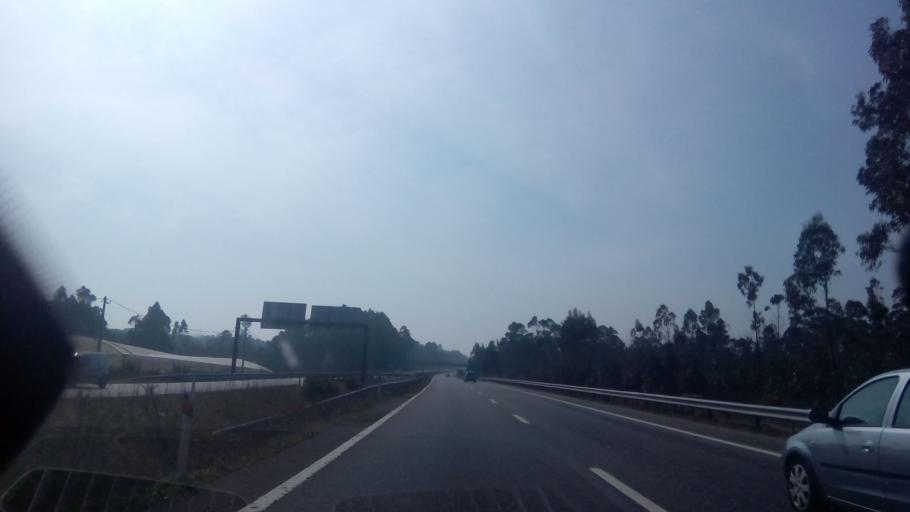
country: PT
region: Porto
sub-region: Povoa de Varzim
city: Pedroso
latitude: 41.4440
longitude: -8.7366
